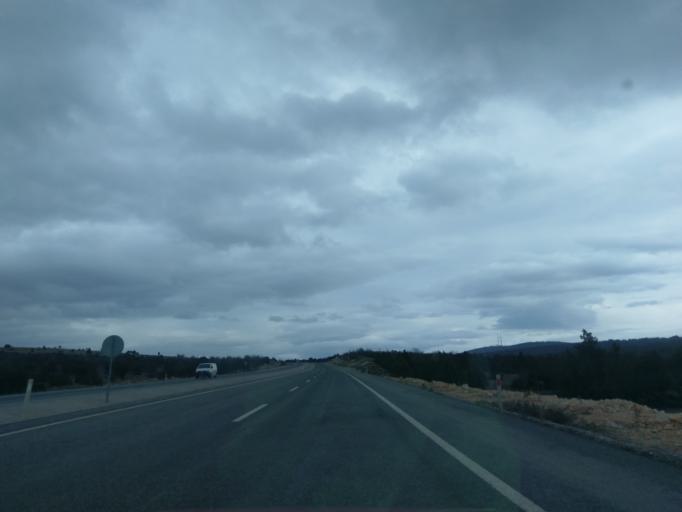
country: TR
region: Kuetahya
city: Aslanapa
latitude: 39.2235
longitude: 29.7477
